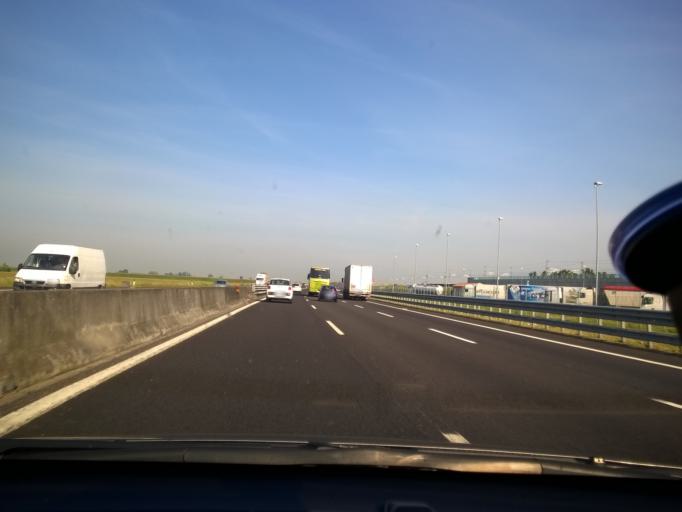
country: IT
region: Emilia-Romagna
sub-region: Provincia di Reggio Emilia
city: Roncocesi
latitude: 44.7429
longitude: 10.5729
